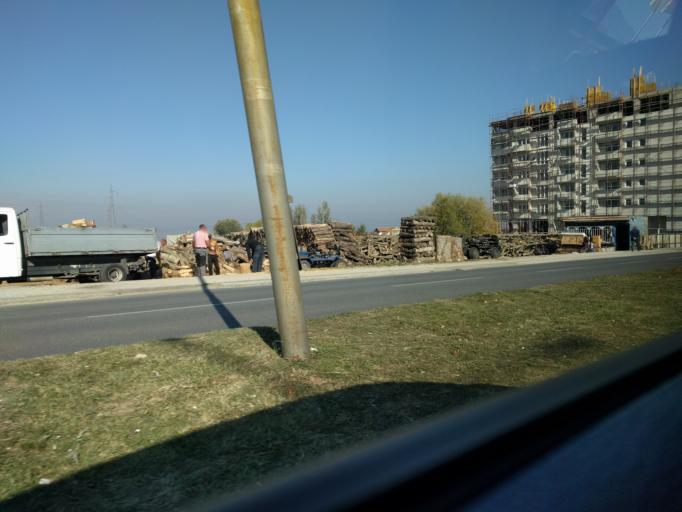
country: XK
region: Prizren
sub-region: Prizren
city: Prizren
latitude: 42.2270
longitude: 20.7528
